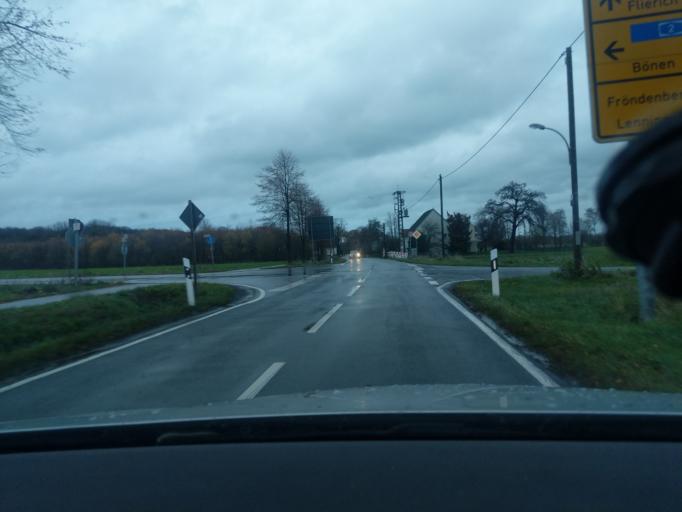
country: DE
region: North Rhine-Westphalia
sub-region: Regierungsbezirk Arnsberg
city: Bonen
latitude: 51.5858
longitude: 7.7883
